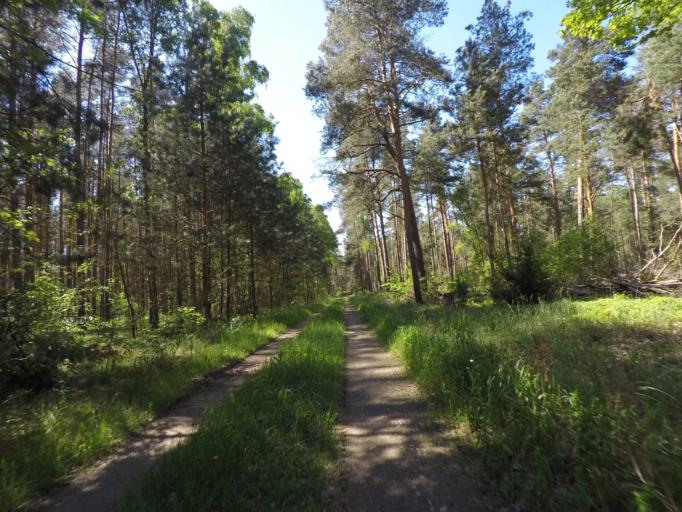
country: DE
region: Brandenburg
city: Eberswalde
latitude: 52.8190
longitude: 13.7575
